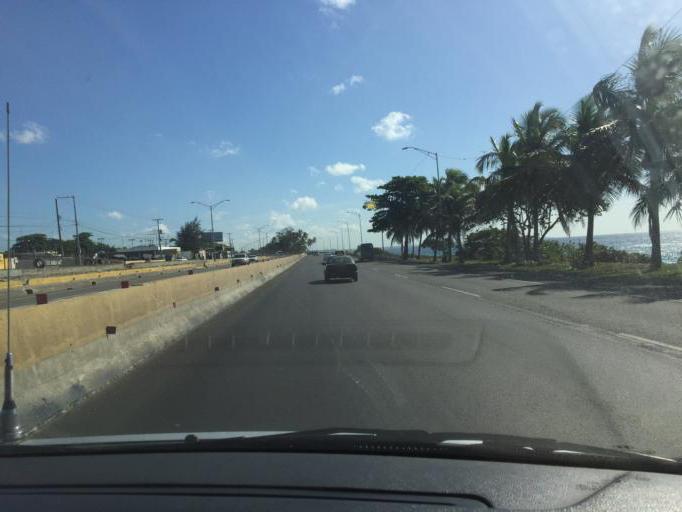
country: DO
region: Santo Domingo
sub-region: Santo Domingo
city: Santo Domingo Este
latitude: 18.4645
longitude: -69.7692
